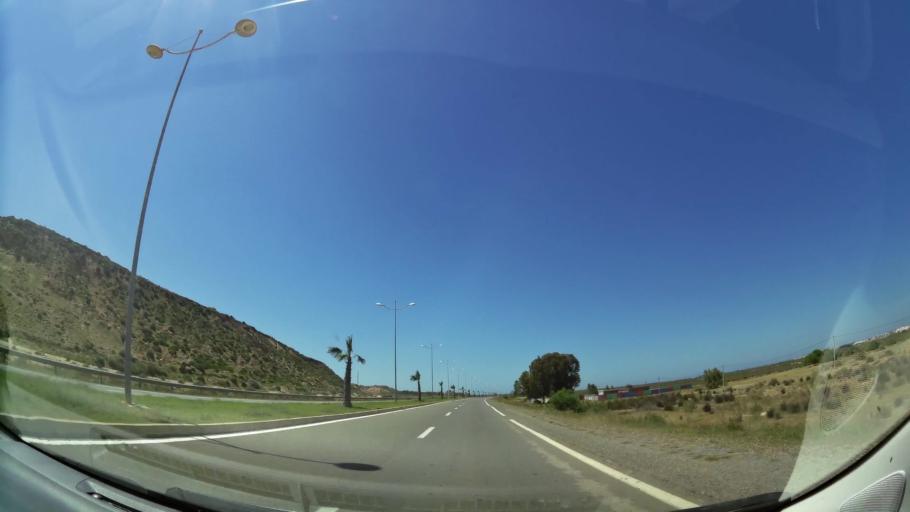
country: MA
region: Oriental
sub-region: Berkane-Taourirt
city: Madagh
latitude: 35.0943
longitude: -2.3145
